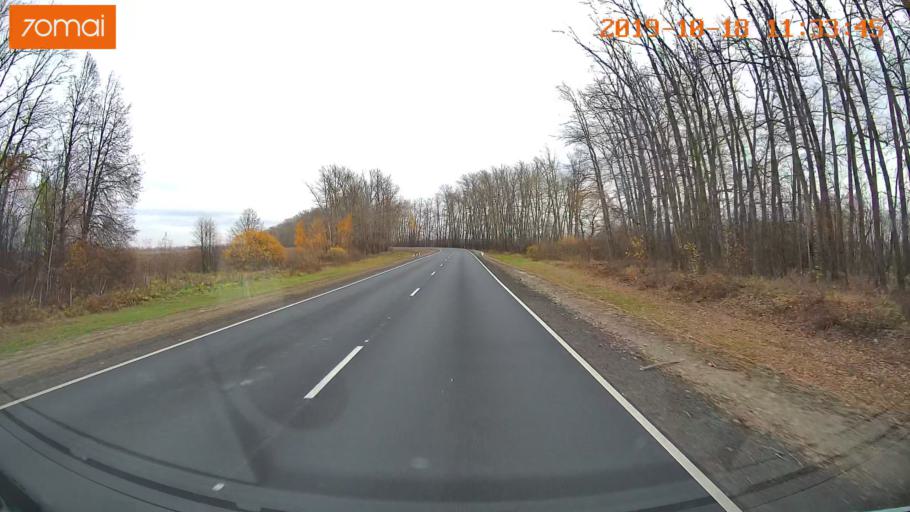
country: RU
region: Rjazan
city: Oktyabr'skiy
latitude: 54.1386
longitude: 38.7481
